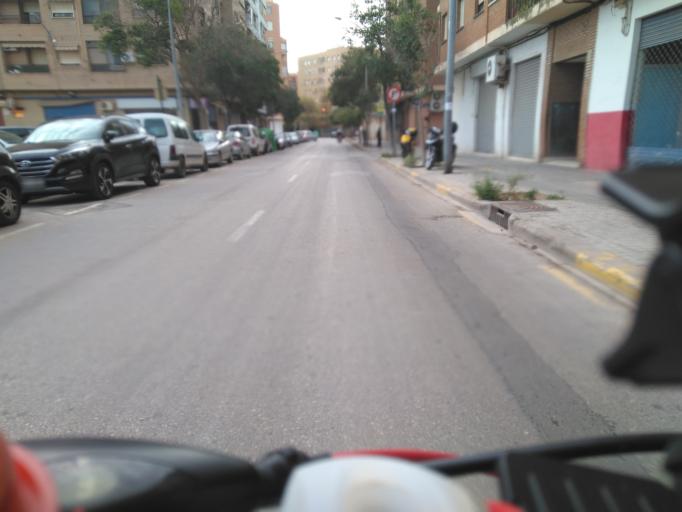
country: ES
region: Valencia
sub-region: Provincia de Valencia
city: Tavernes Blanques
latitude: 39.4920
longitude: -0.3874
